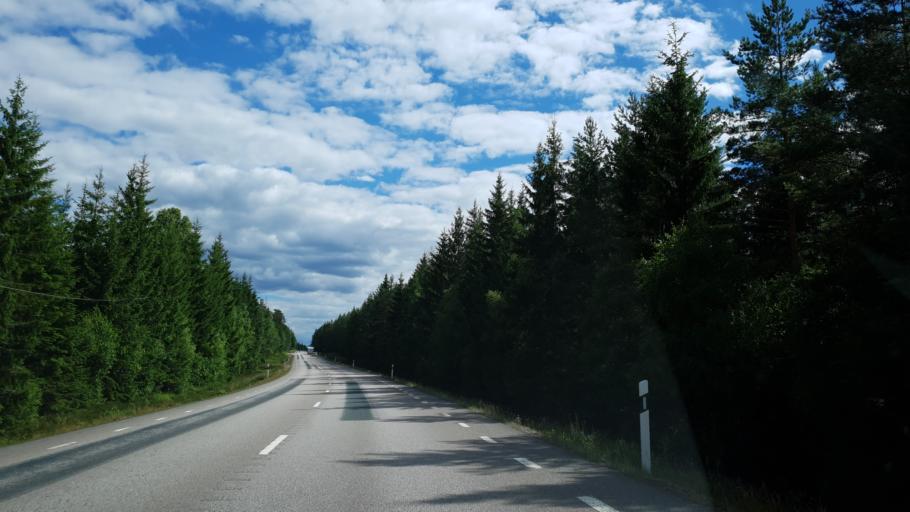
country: SE
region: Kronoberg
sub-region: Uppvidinge Kommun
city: Lenhovda
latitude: 56.8805
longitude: 15.3786
